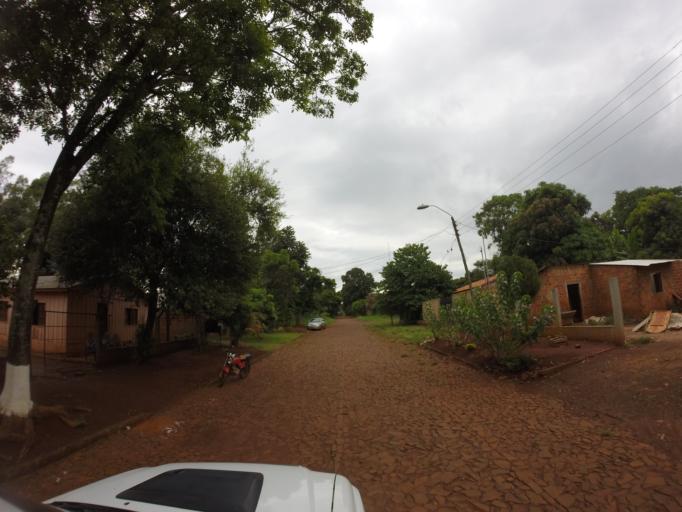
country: PY
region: Alto Parana
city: Ciudad del Este
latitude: -25.4163
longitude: -54.6536
